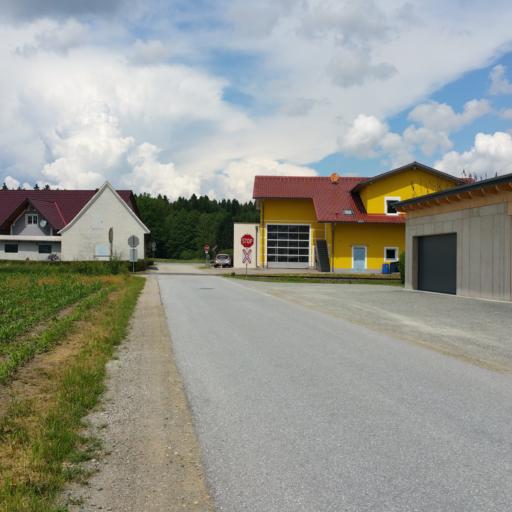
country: AT
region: Styria
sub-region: Politischer Bezirk Leibnitz
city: Gleinstatten
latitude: 46.7482
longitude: 15.3492
